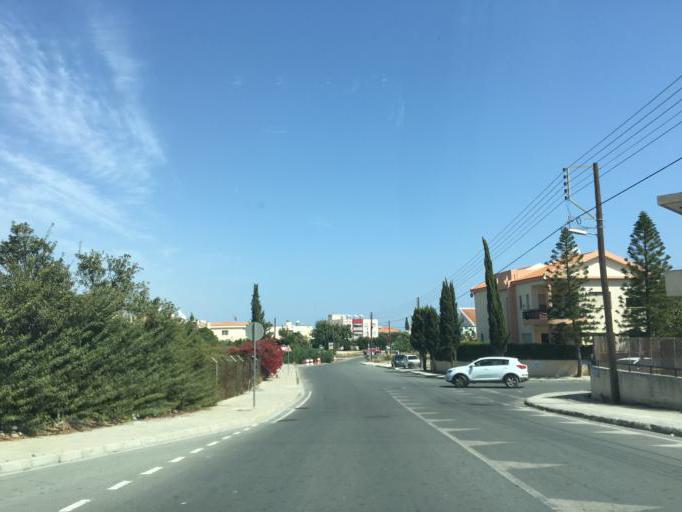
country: CY
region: Limassol
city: Mouttagiaka
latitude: 34.7041
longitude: 33.0743
